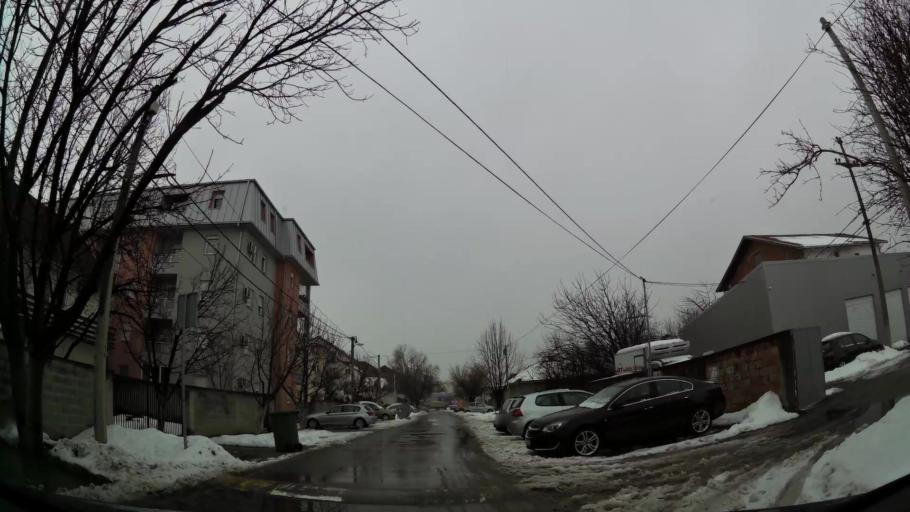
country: RS
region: Central Serbia
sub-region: Belgrade
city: Zemun
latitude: 44.8512
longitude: 20.3634
